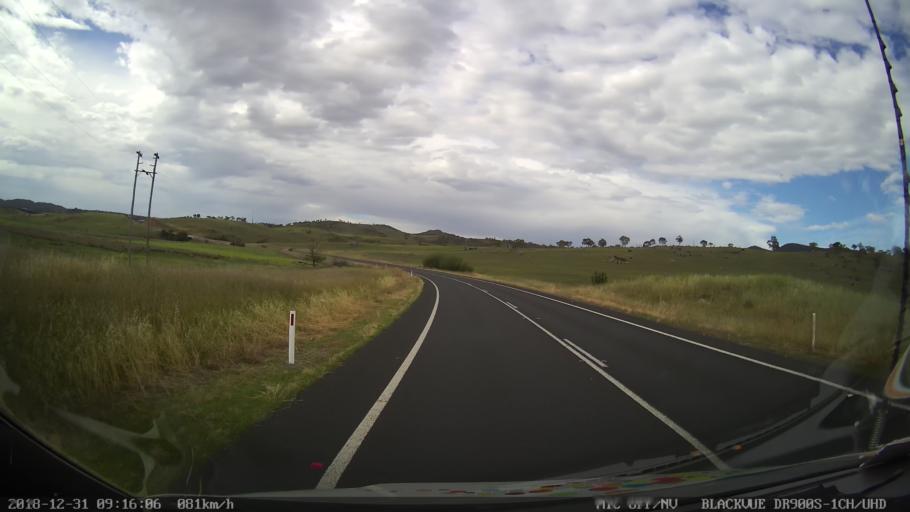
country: AU
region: New South Wales
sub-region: Snowy River
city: Jindabyne
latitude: -36.3923
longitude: 148.5943
